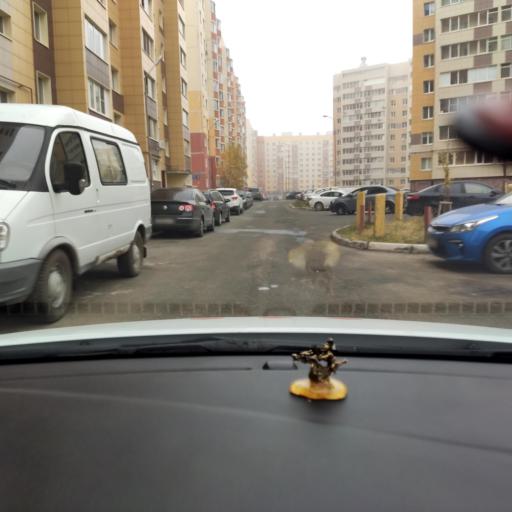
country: RU
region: Tatarstan
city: Osinovo
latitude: 55.8697
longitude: 48.8794
